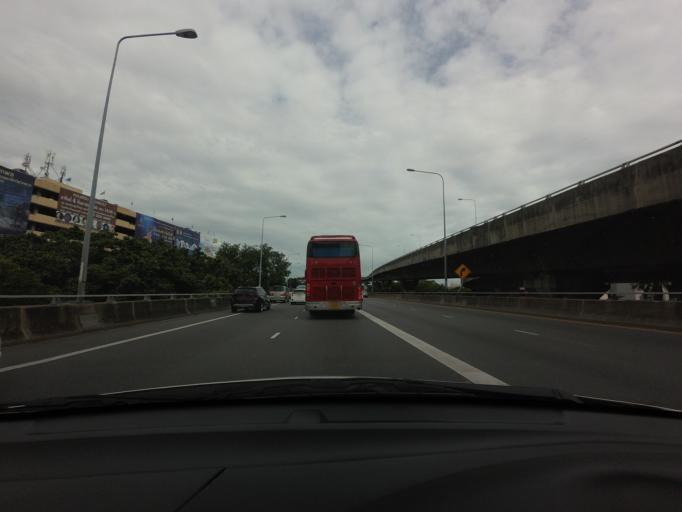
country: TH
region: Bangkok
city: Ratchathewi
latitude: 13.7708
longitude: 100.5334
